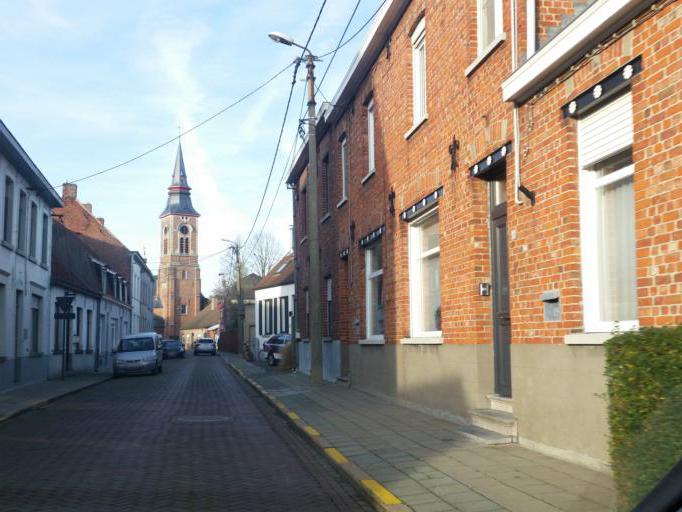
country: BE
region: Flanders
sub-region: Provincie West-Vlaanderen
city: Beernem
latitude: 51.1692
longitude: 3.3422
